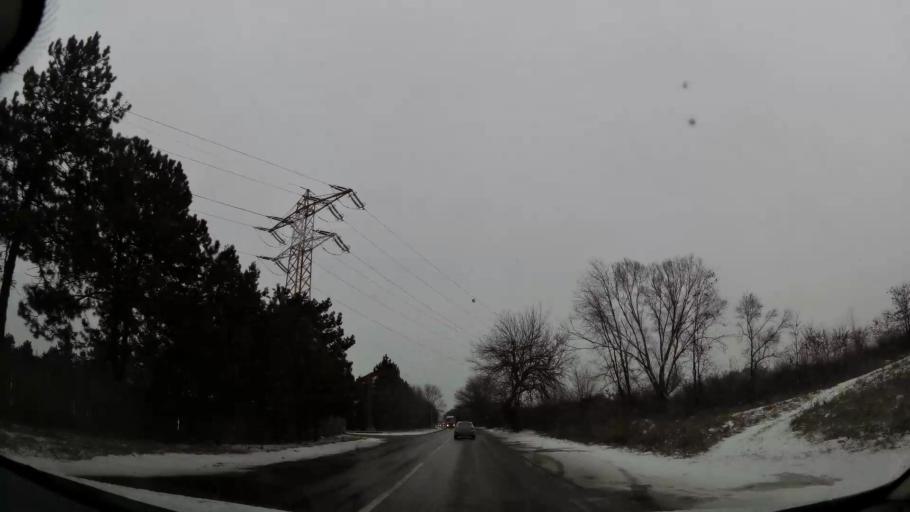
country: RO
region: Dambovita
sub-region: Comuna Ulmi
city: Ulmi
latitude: 44.8985
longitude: 25.5047
